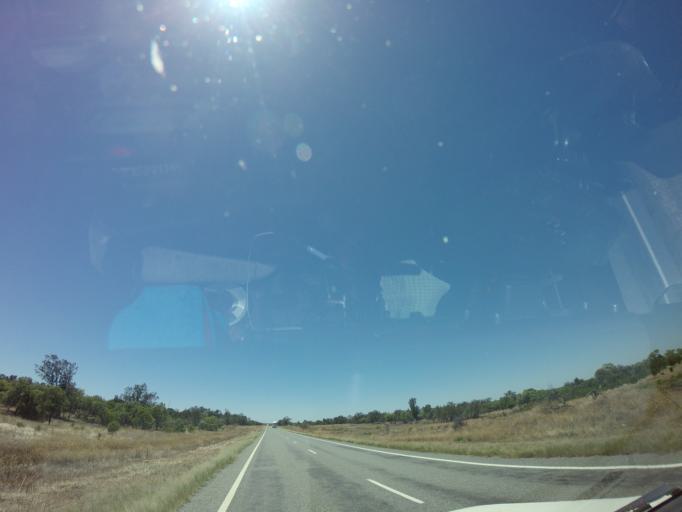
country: AU
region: New South Wales
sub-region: Cobar
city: Cobar
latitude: -31.5808
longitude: 144.8227
